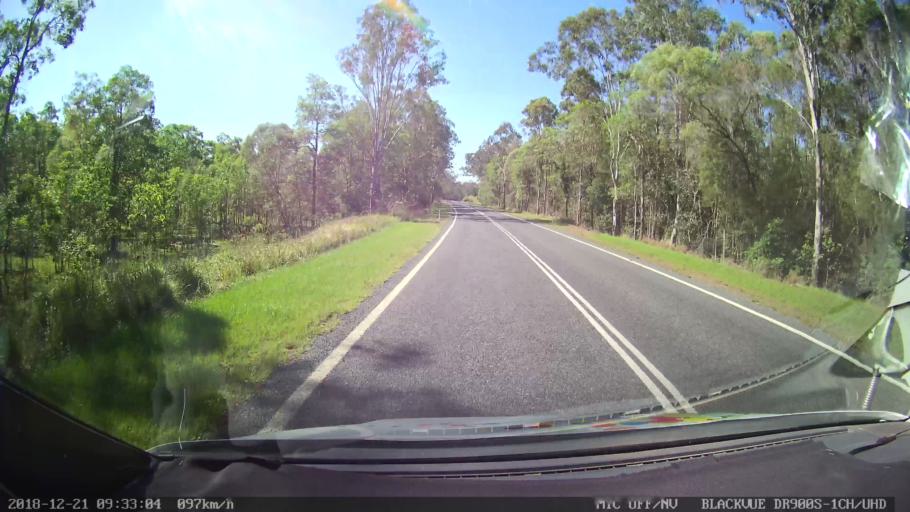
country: AU
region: New South Wales
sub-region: Clarence Valley
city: Grafton
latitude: -29.4792
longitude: 152.9762
